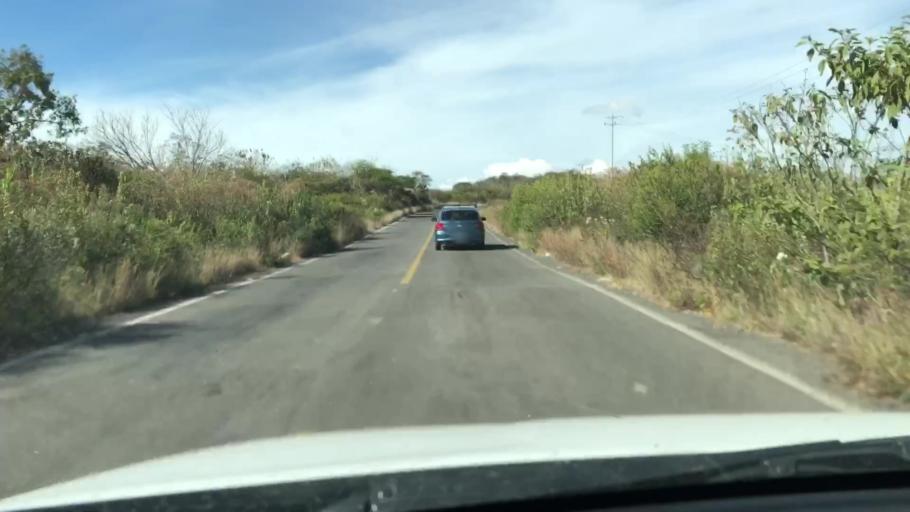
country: MX
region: Jalisco
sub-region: Zacoalco de Torres
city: Barranca de Otates (Barranca de Otatan)
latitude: 20.2103
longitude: -103.6944
